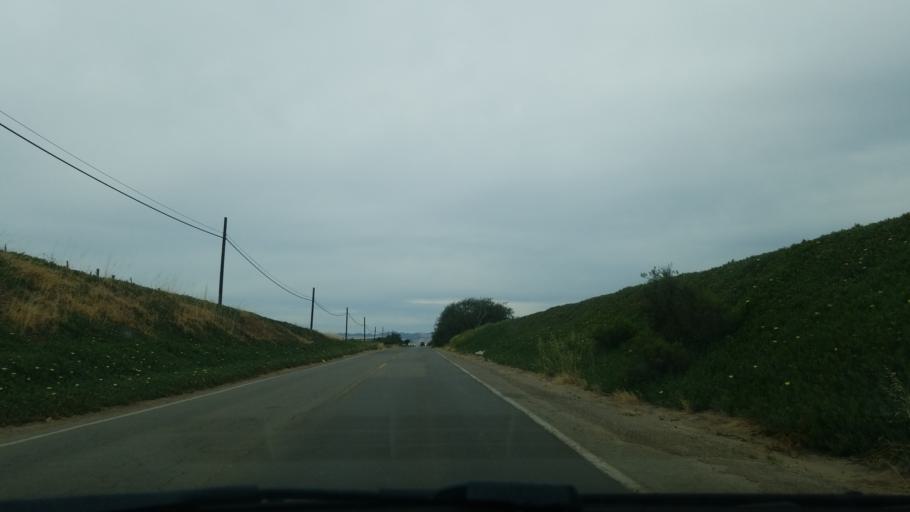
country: US
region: California
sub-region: Santa Barbara County
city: Santa Maria
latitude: 34.9141
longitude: -120.4840
